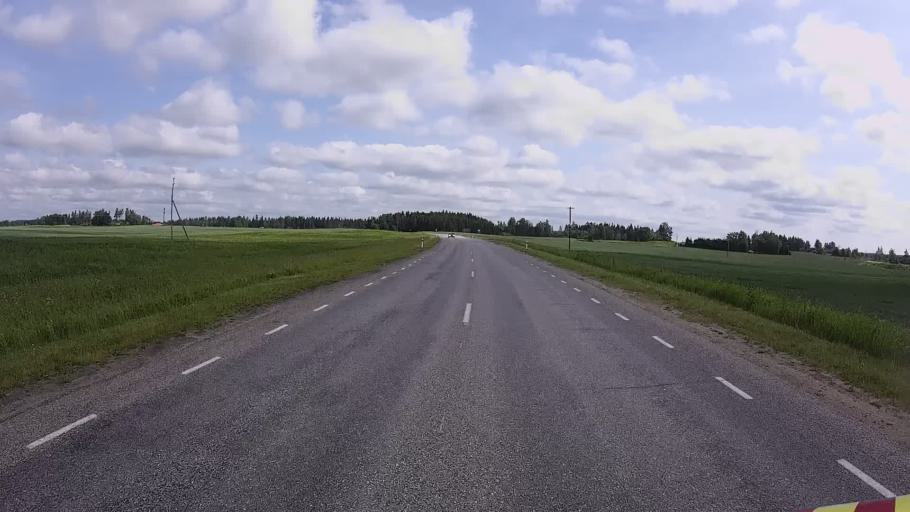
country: EE
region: Vorumaa
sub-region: Voru linn
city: Voru
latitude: 57.8664
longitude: 26.9238
